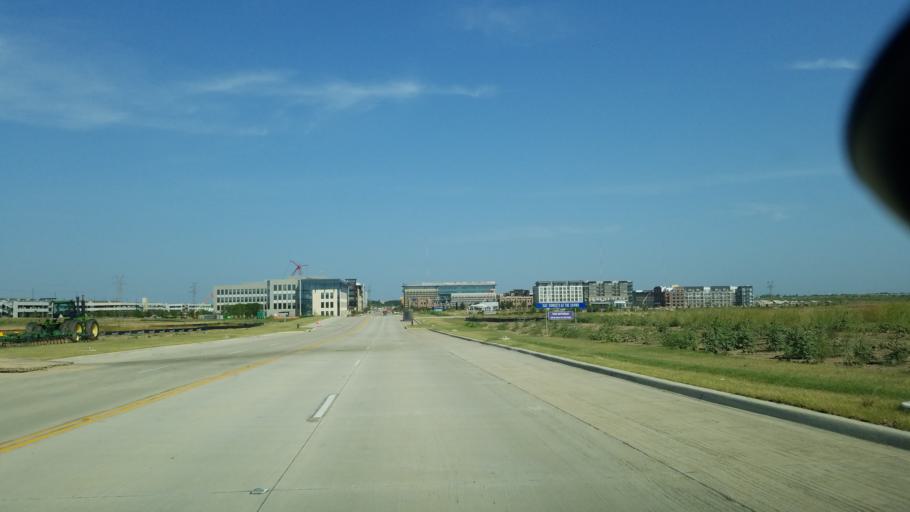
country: US
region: Texas
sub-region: Dallas County
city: Coppell
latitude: 32.9330
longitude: -96.9783
